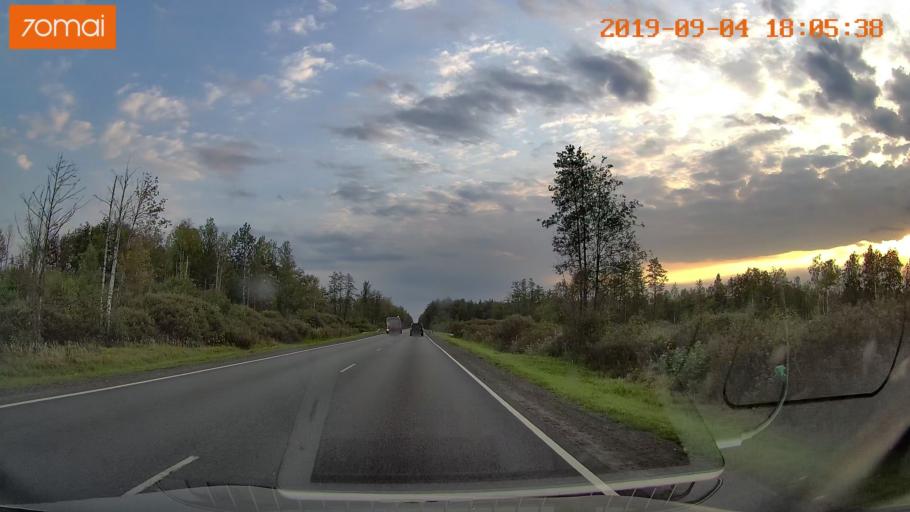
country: RU
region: Moskovskaya
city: Il'inskiy Pogost
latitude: 55.4393
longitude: 38.8242
